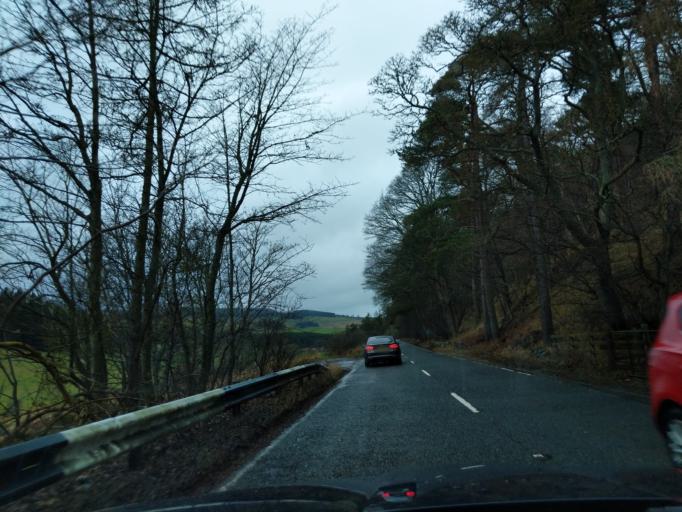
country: GB
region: Scotland
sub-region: The Scottish Borders
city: Galashiels
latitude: 55.6461
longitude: -2.8561
